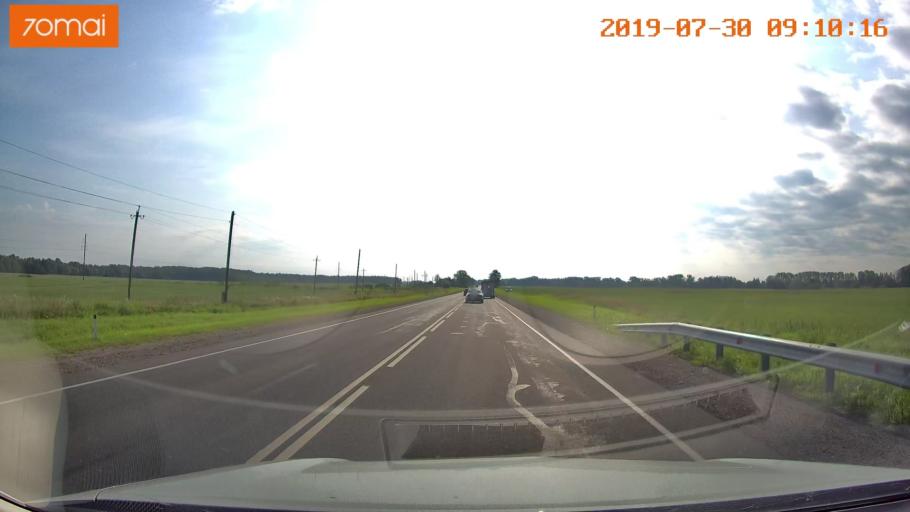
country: RU
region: Kaliningrad
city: Nesterov
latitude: 54.6121
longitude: 22.4231
